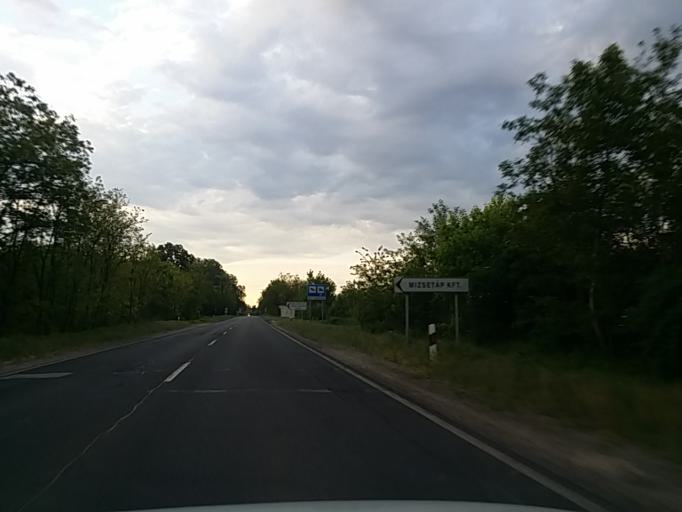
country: HU
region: Bacs-Kiskun
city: Lajosmizse
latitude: 47.0543
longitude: 19.5180
